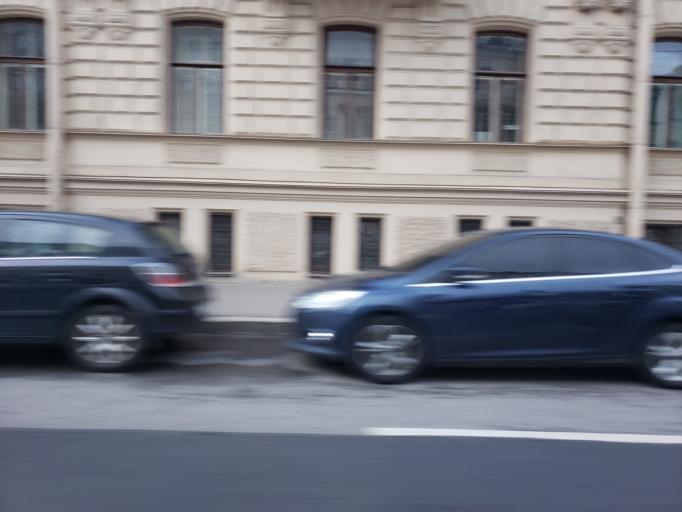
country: RU
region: St.-Petersburg
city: Vasyl'evsky Ostrov
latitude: 59.9374
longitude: 30.2817
